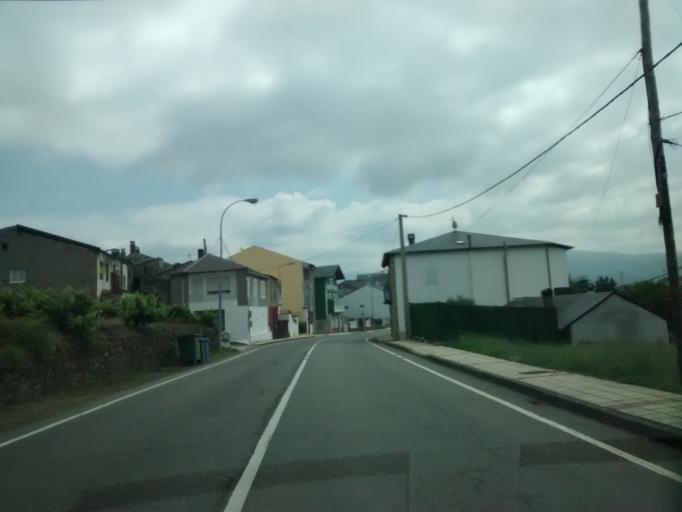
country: ES
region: Galicia
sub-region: Provincia de Ourense
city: Petin
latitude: 42.3465
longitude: -7.1690
